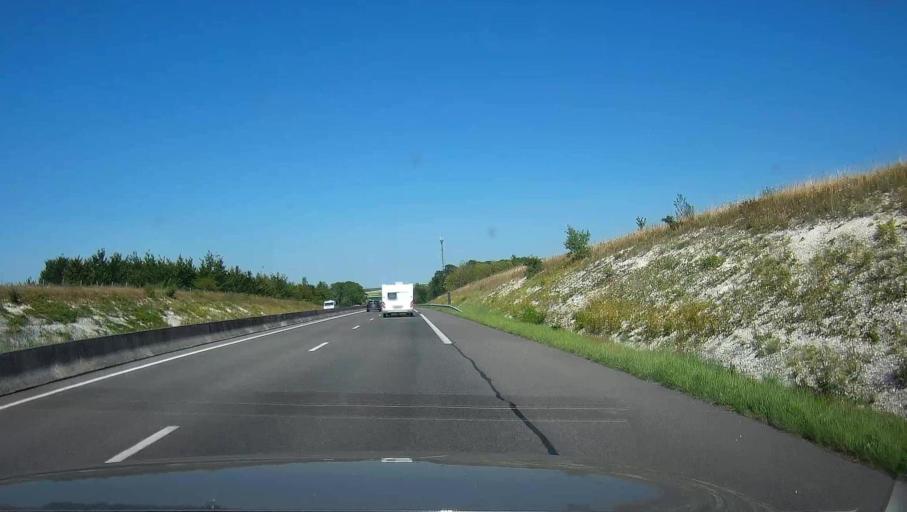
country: FR
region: Champagne-Ardenne
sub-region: Departement de l'Aube
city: Mailly-le-Camp
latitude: 48.6557
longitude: 4.1746
